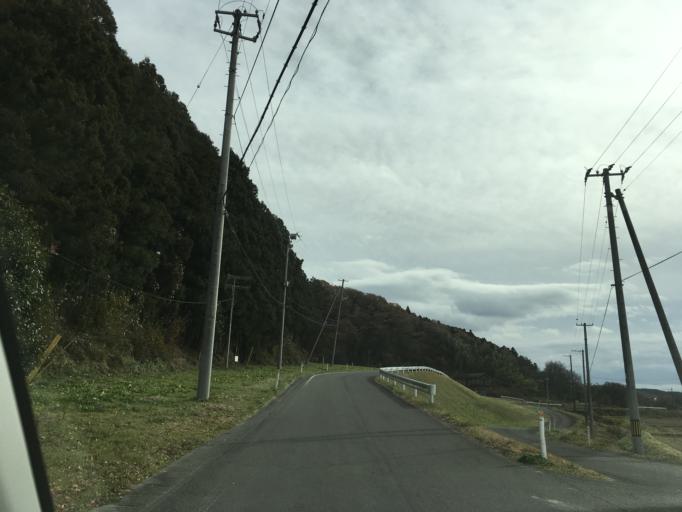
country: JP
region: Iwate
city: Ichinoseki
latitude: 38.7678
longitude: 141.2730
